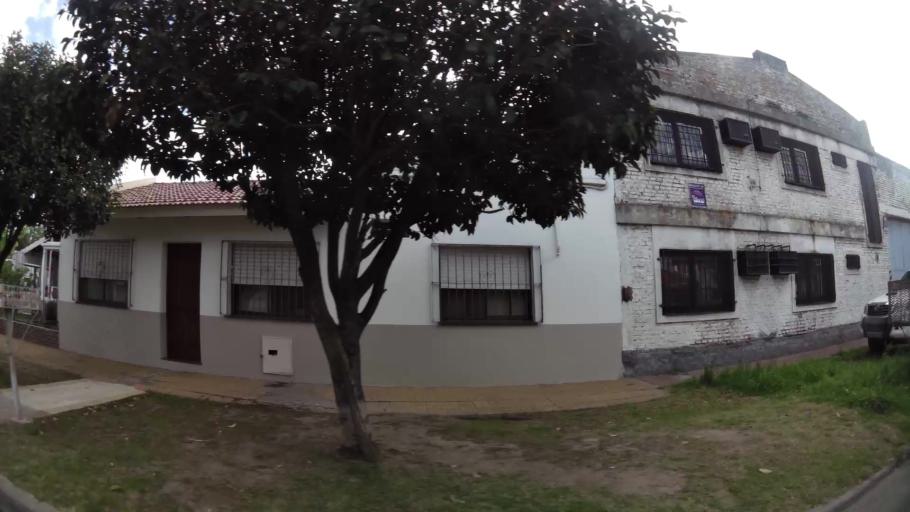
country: AR
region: Buenos Aires
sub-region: Partido de Avellaneda
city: Avellaneda
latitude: -34.6924
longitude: -58.3476
